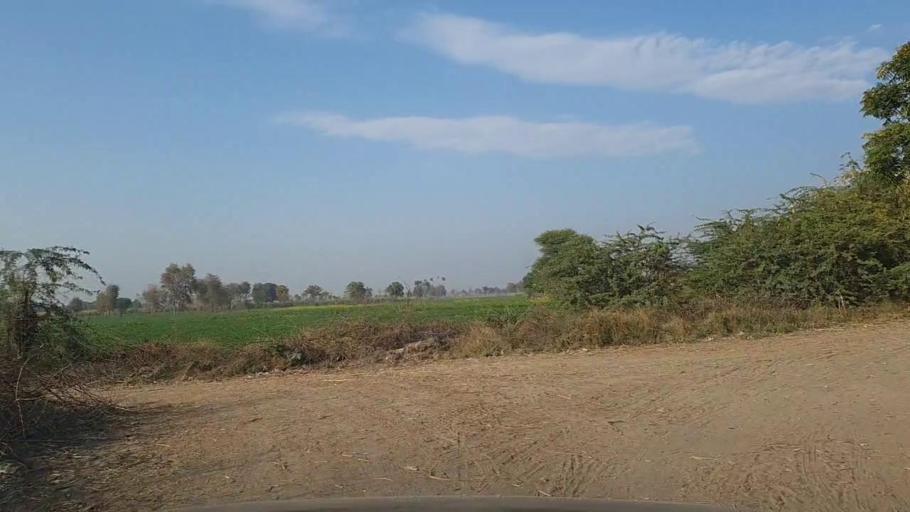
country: PK
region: Sindh
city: Daur
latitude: 26.4151
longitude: 68.4372
